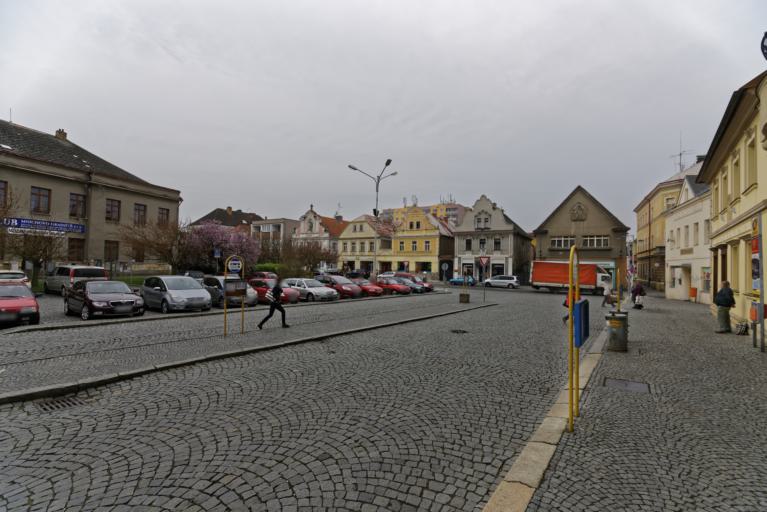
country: CZ
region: Central Bohemia
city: Mnichovo Hradiste
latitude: 50.5232
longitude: 14.9743
